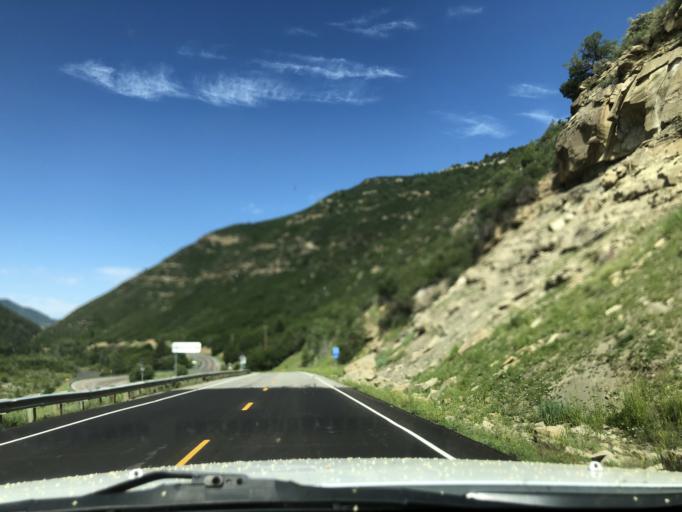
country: US
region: Colorado
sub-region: Delta County
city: Paonia
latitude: 38.9413
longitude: -107.3594
